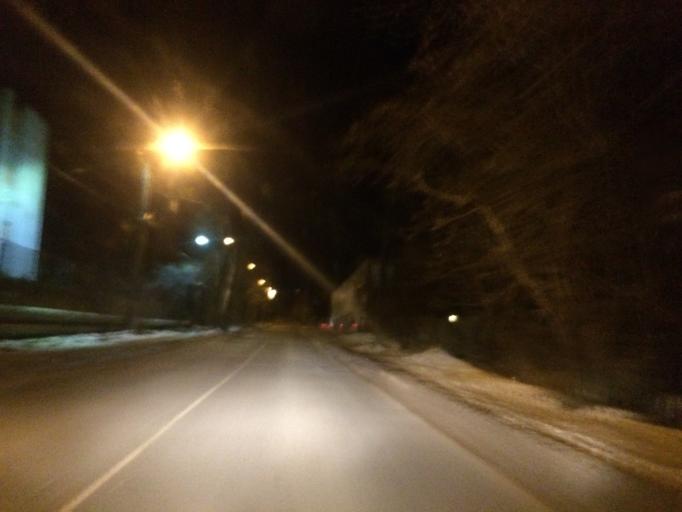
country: RU
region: Tula
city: Mendeleyevskiy
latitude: 54.1641
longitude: 37.5657
